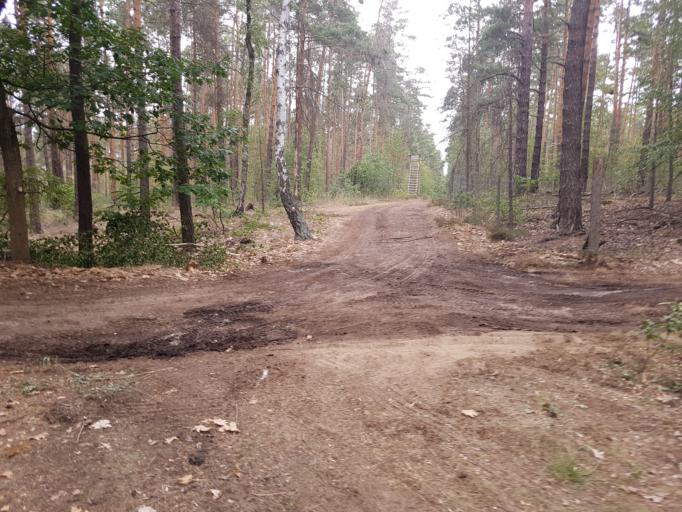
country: DE
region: Brandenburg
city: Finsterwalde
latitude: 51.6288
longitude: 13.6617
